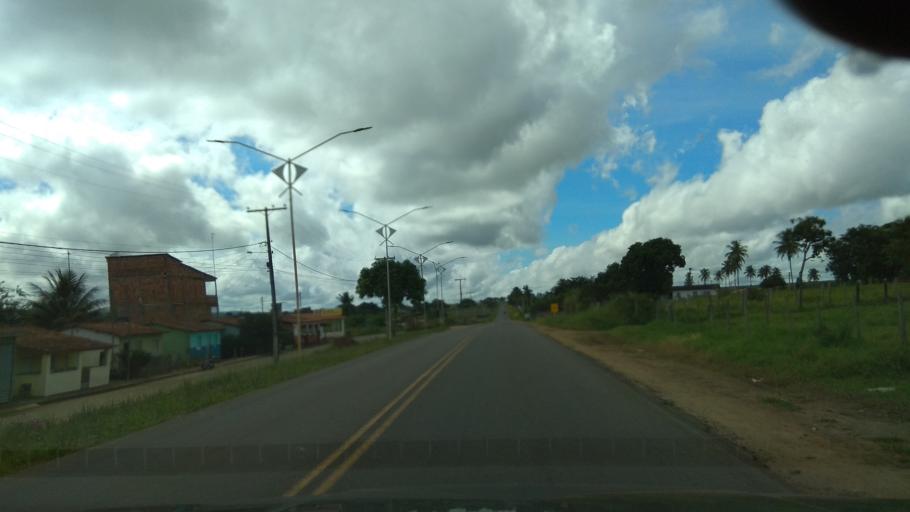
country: BR
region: Bahia
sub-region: Mutuipe
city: Mutuipe
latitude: -13.1653
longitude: -39.4072
